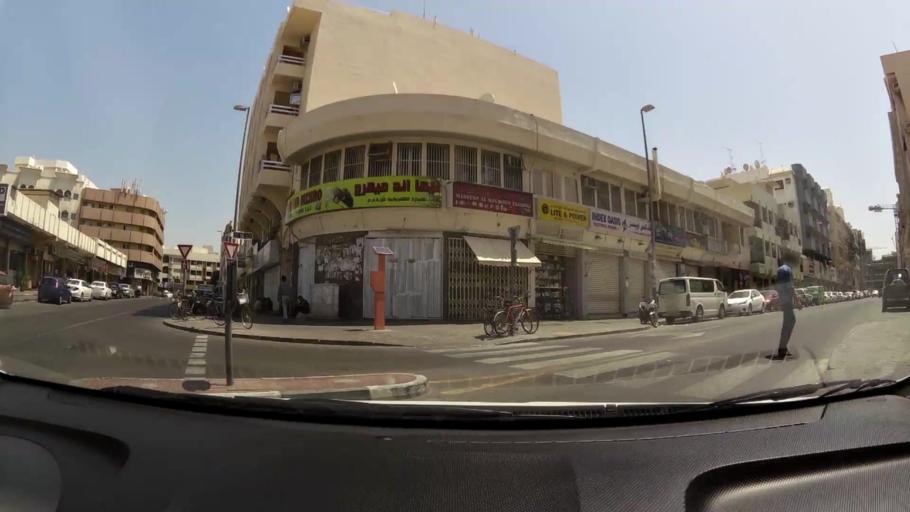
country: AE
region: Ash Shariqah
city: Sharjah
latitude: 25.2738
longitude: 55.3135
